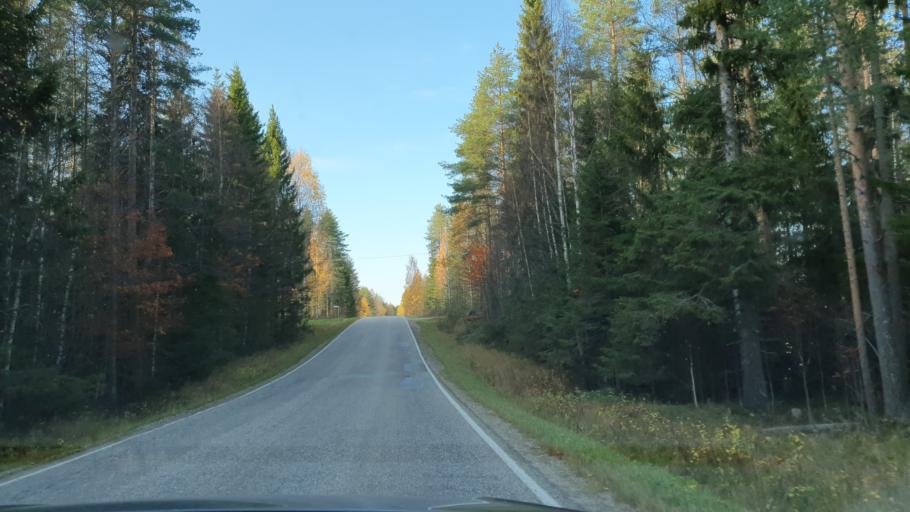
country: FI
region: Kainuu
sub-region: Kehys-Kainuu
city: Kuhmo
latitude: 64.1790
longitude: 29.4498
